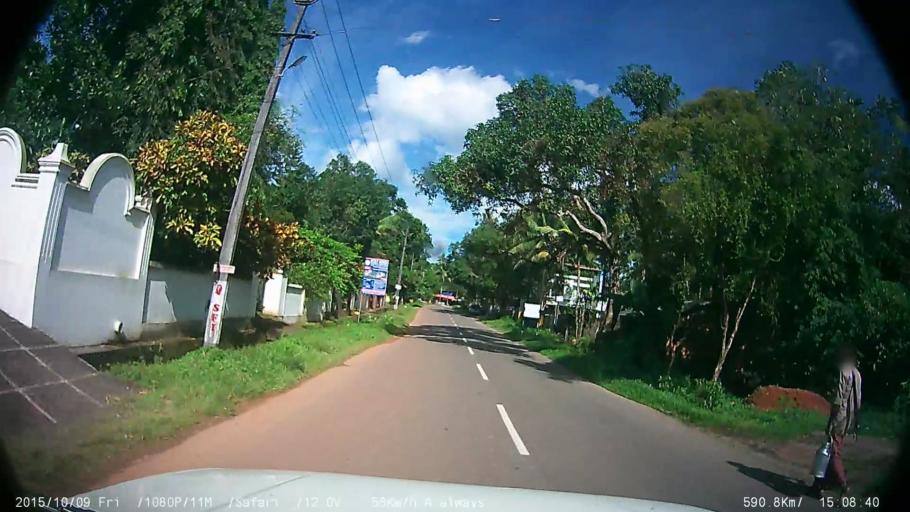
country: IN
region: Kerala
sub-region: Ernakulam
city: Piravam
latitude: 9.8866
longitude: 76.5675
